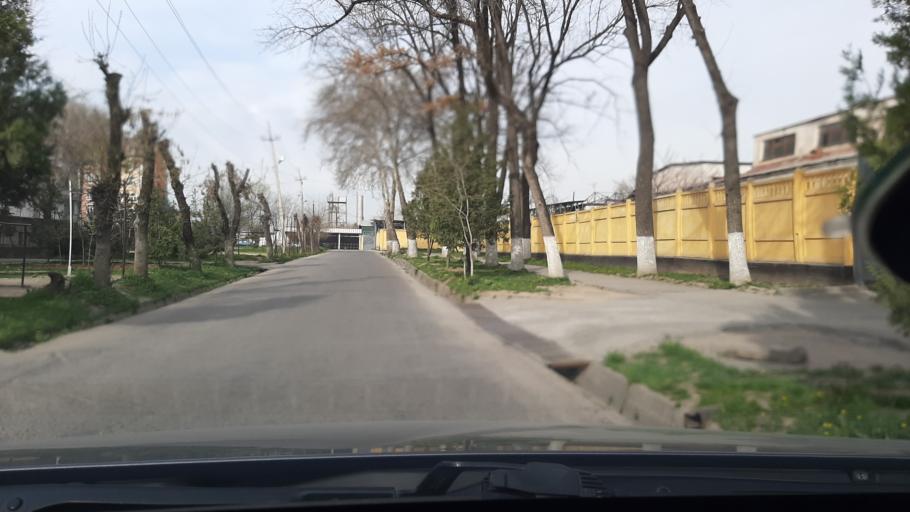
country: TJ
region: Dushanbe
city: Dushanbe
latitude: 38.5705
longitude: 68.7621
